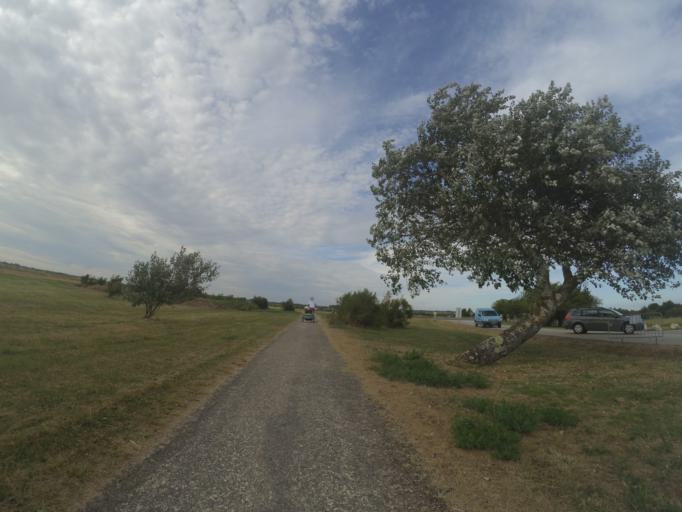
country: FR
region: Poitou-Charentes
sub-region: Departement de la Charente-Maritime
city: Meschers-sur-Gironde
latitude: 45.5376
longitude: -0.9058
